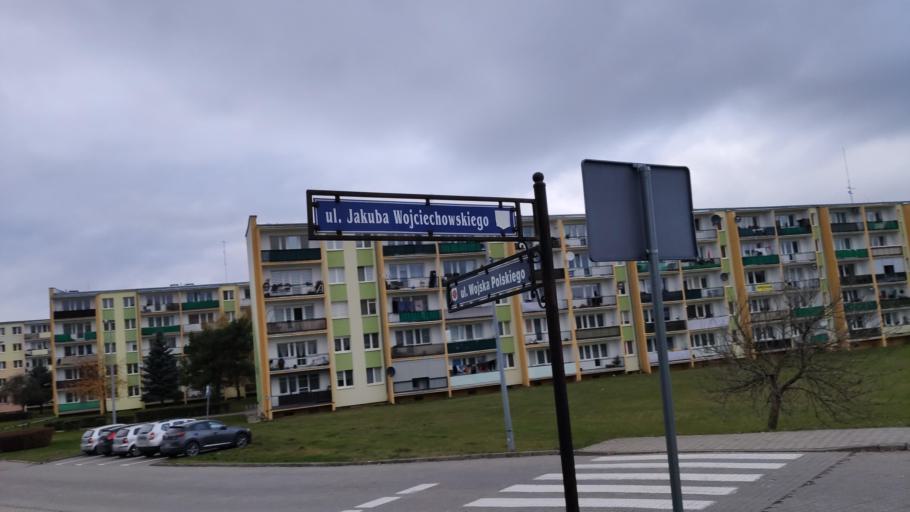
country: PL
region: Kujawsko-Pomorskie
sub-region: Powiat zninski
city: Barcin
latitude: 52.8549
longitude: 17.9458
